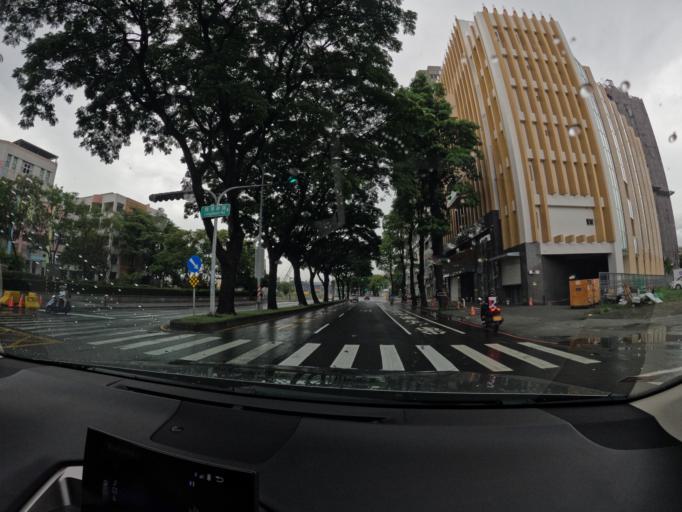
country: TW
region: Kaohsiung
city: Kaohsiung
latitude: 22.6563
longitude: 120.3108
